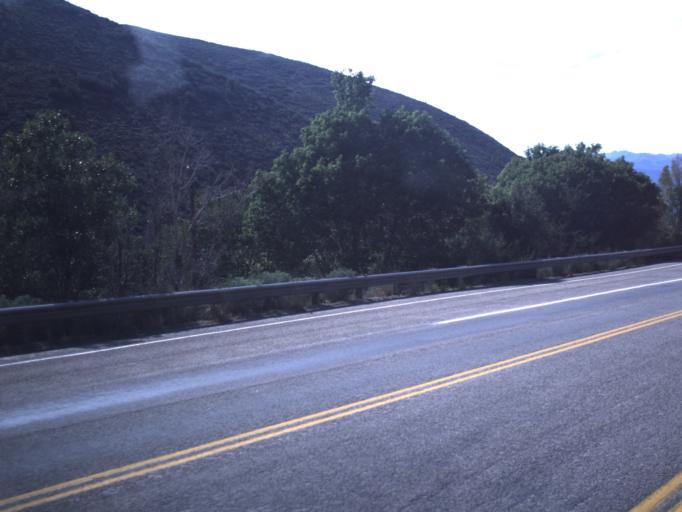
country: US
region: Utah
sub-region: Wasatch County
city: Heber
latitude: 40.4490
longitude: -111.3684
